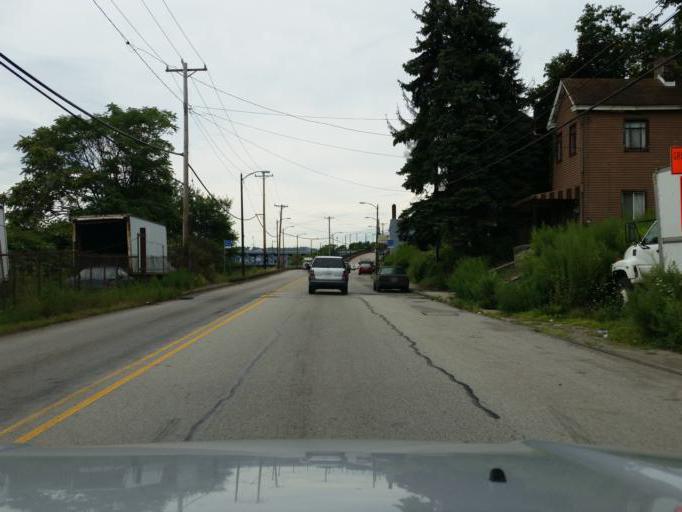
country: US
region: Pennsylvania
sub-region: Allegheny County
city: Whitaker
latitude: 40.4061
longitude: -79.8867
